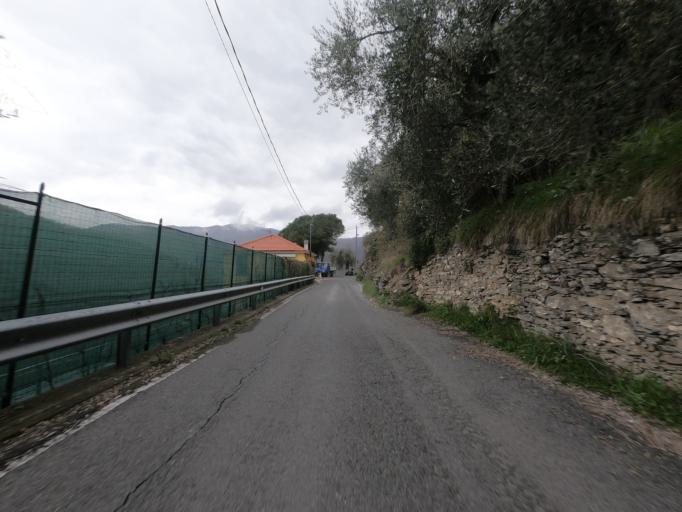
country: IT
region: Liguria
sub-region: Provincia di Savona
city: Testico
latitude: 44.0297
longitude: 8.0210
